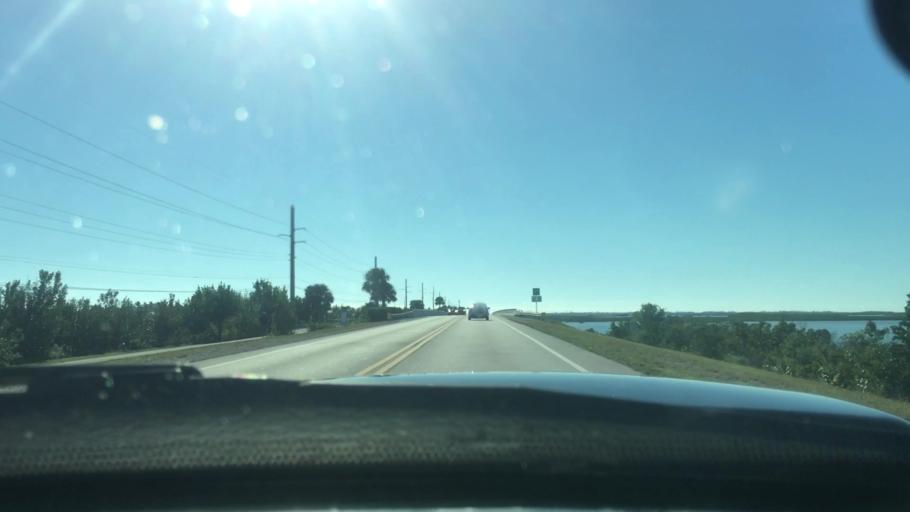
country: US
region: Florida
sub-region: Monroe County
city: Big Coppitt Key
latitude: 24.6273
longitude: -81.5962
